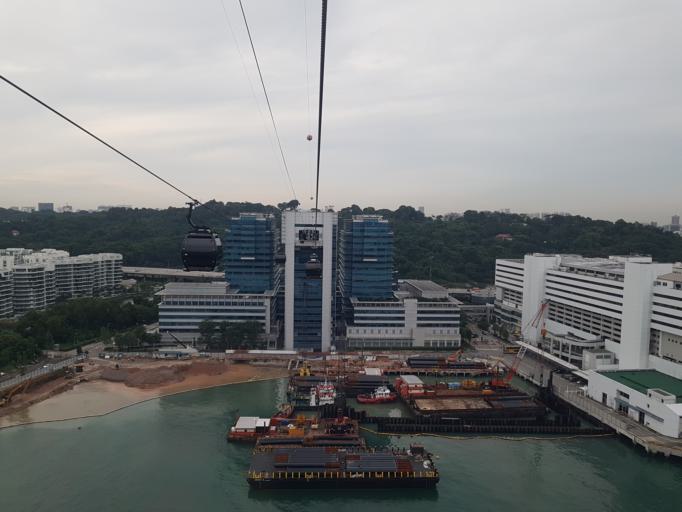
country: SG
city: Singapore
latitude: 1.2614
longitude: 103.8184
